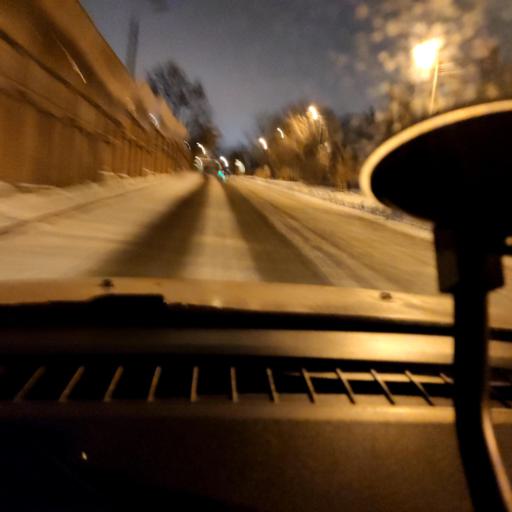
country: RU
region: Samara
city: Samara
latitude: 53.2772
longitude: 50.1893
